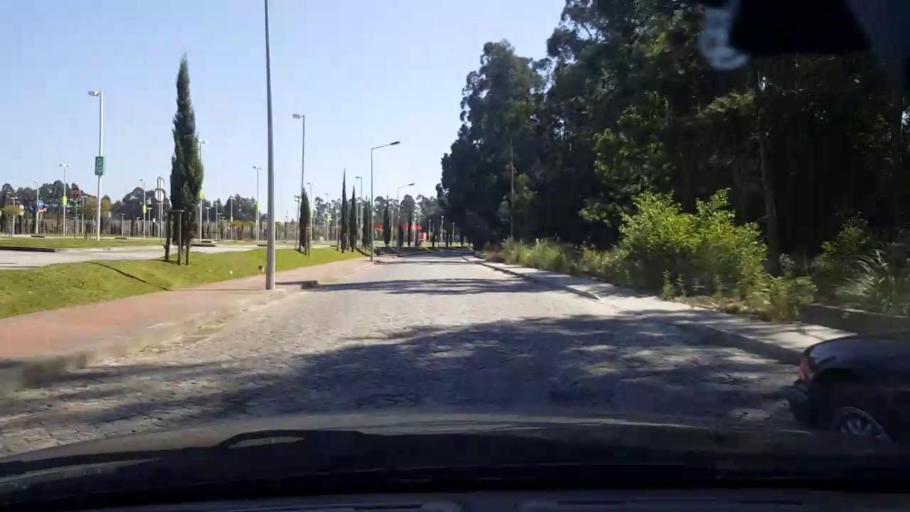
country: PT
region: Porto
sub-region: Matosinhos
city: Lavra
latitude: 41.2991
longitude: -8.7093
